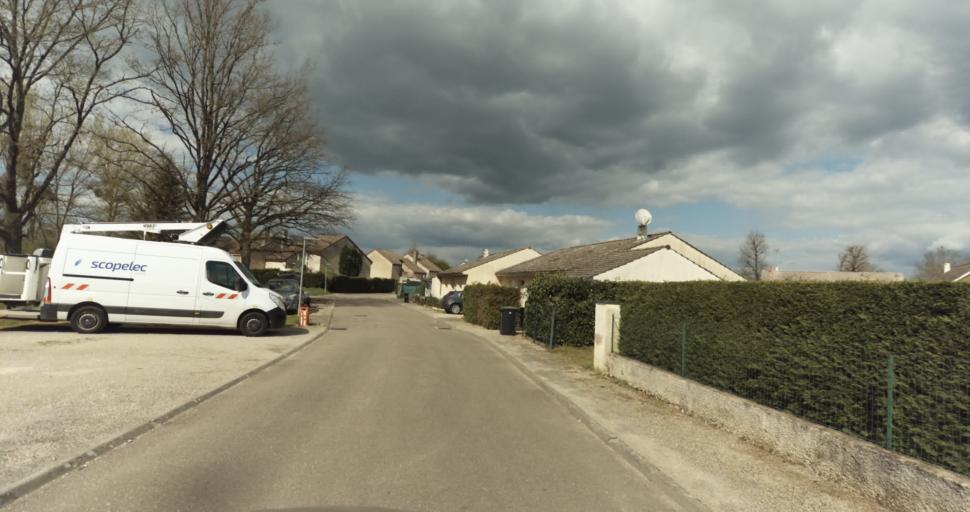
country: FR
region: Bourgogne
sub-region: Departement de la Cote-d'Or
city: Auxonne
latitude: 47.1887
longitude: 5.4126
